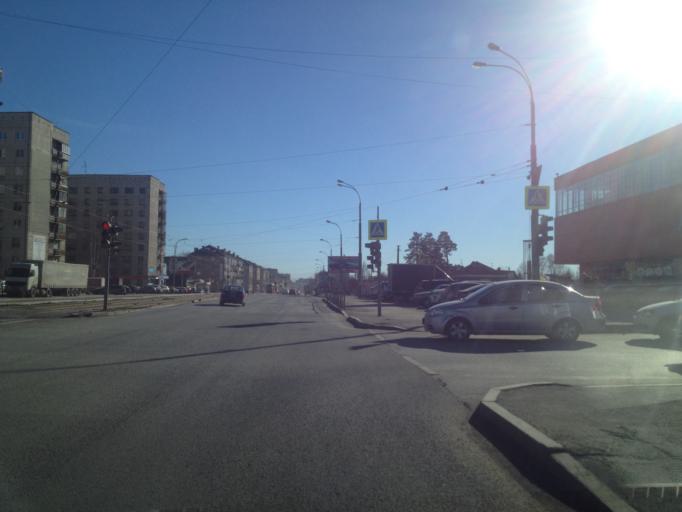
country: RU
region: Sverdlovsk
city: Yekaterinburg
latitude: 56.8925
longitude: 60.5713
